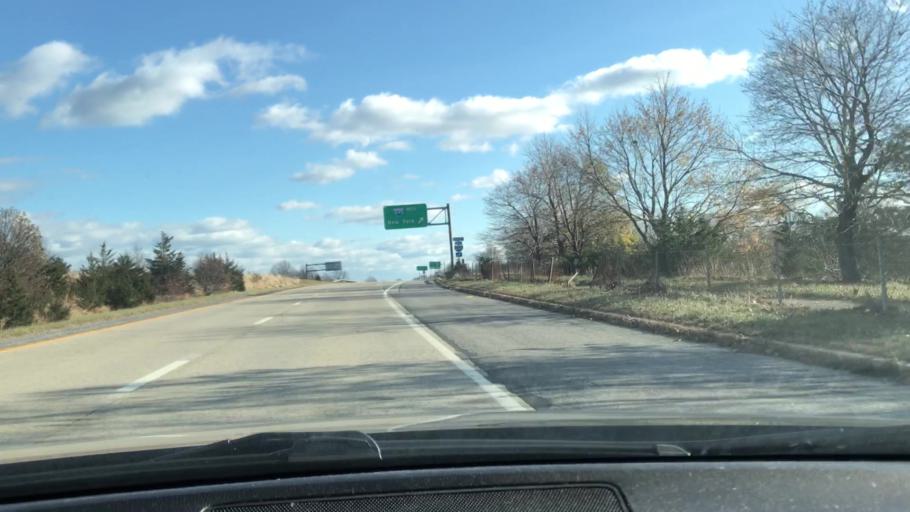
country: US
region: New York
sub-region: Suffolk County
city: Calverton
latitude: 40.9227
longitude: -72.7269
